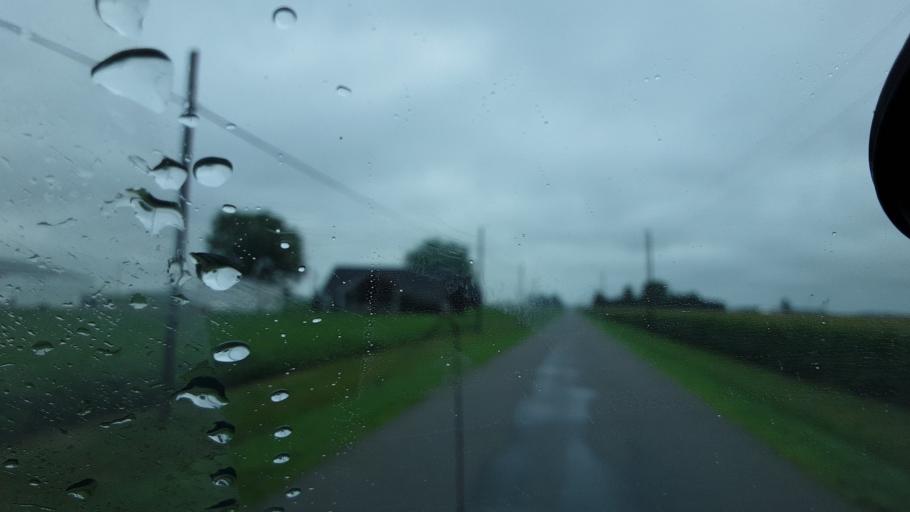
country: US
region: Ohio
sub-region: Mercer County
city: Rockford
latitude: 40.7566
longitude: -84.6365
